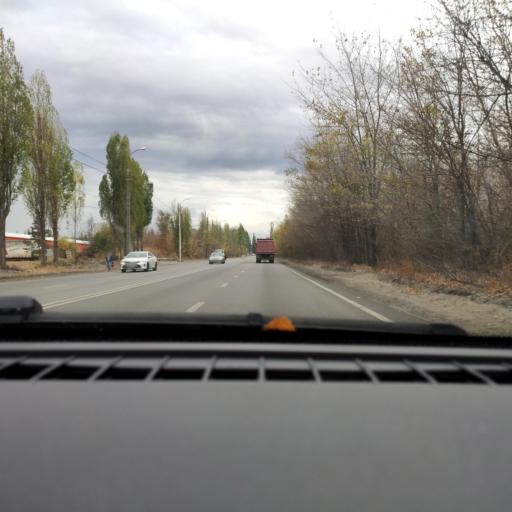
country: RU
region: Voronezj
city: Maslovka
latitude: 51.6061
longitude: 39.2551
